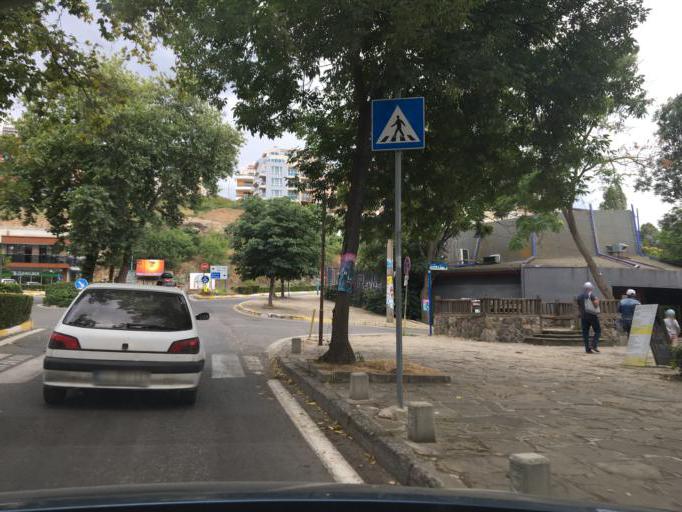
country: BG
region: Burgas
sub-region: Obshtina Sozopol
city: Sozopol
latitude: 42.4196
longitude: 27.6934
